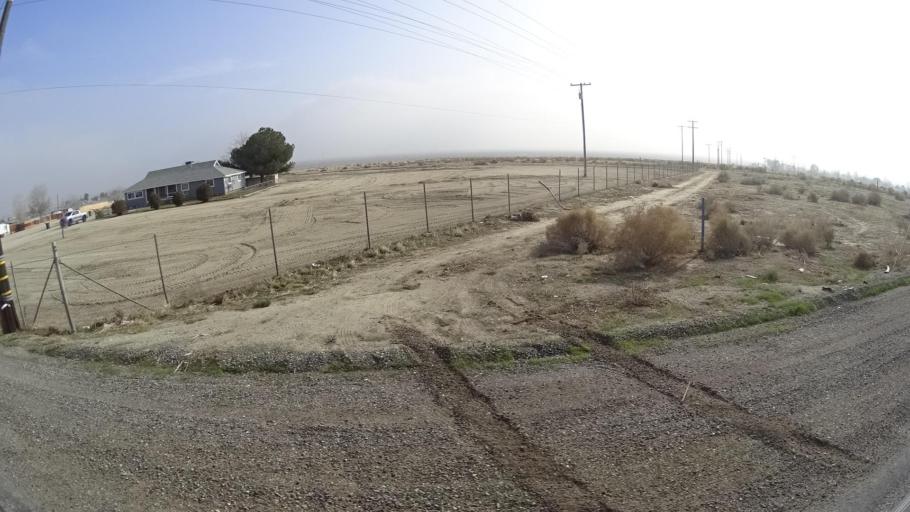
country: US
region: California
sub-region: Kern County
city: Ford City
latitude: 35.2287
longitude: -119.3767
